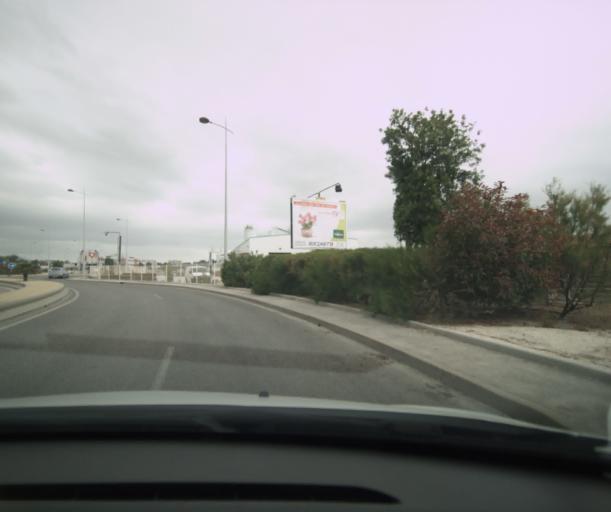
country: FR
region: Provence-Alpes-Cote d'Azur
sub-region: Departement du Var
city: La Garde
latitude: 43.1361
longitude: 6.0330
